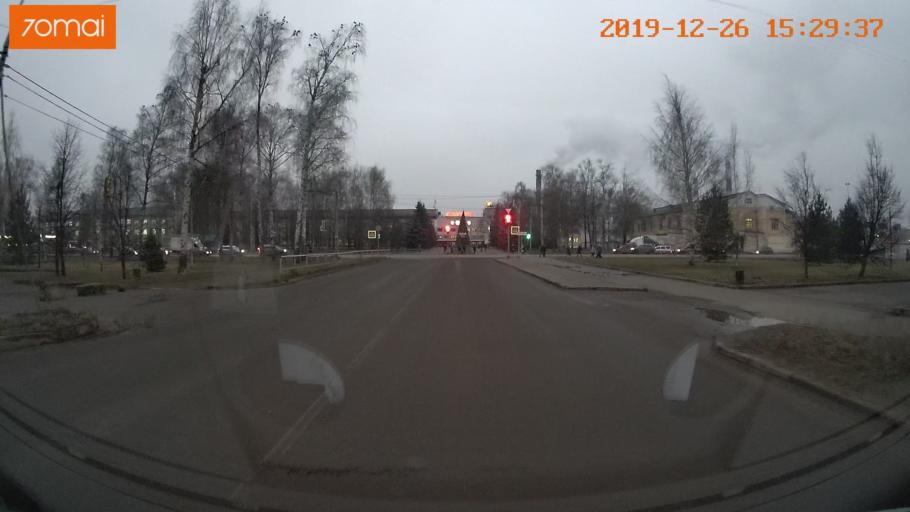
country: RU
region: Jaroslavl
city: Rybinsk
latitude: 58.0558
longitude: 38.8165
